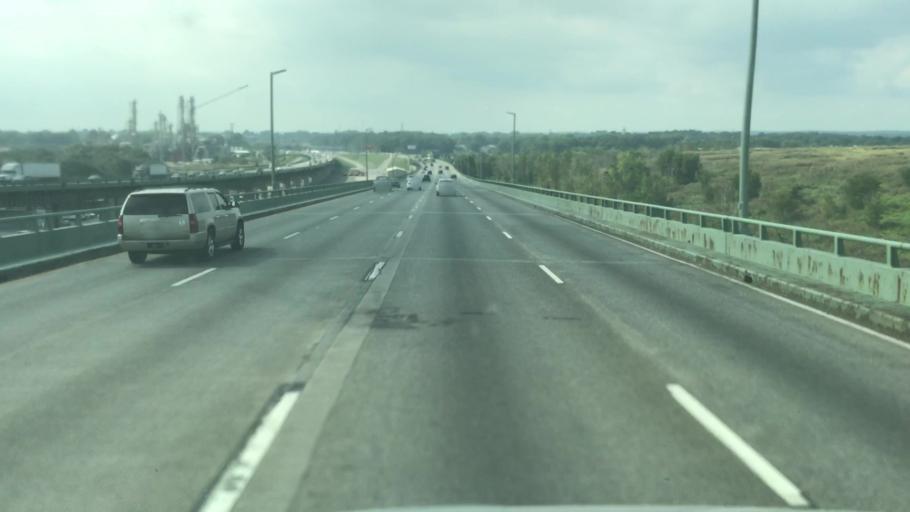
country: US
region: New Jersey
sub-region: Salem County
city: Pennsville
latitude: 39.6928
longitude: -75.5294
